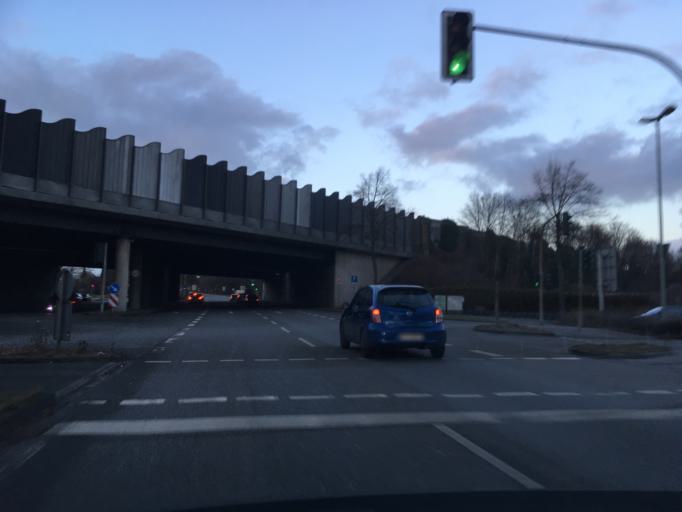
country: DE
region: North Rhine-Westphalia
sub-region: Regierungsbezirk Munster
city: Bottrop
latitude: 51.5497
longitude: 6.9165
